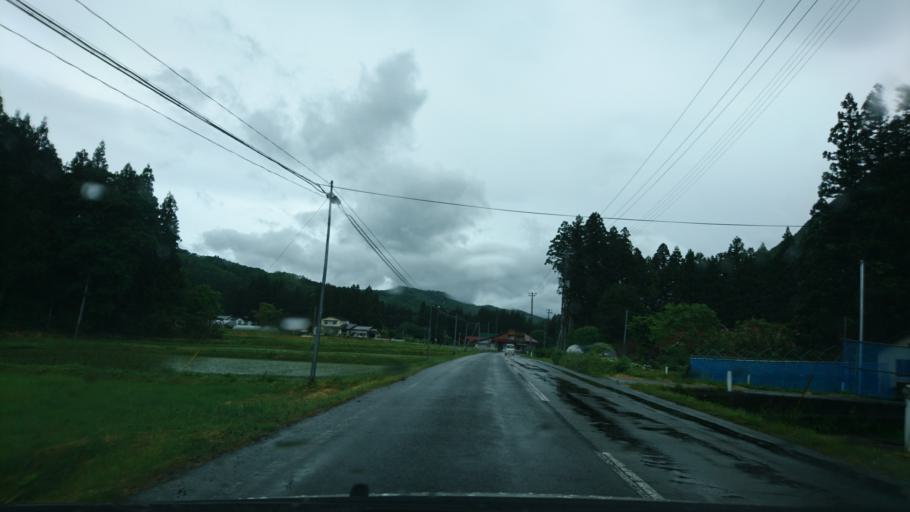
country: JP
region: Iwate
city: Ichinoseki
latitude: 38.9834
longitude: 140.9139
